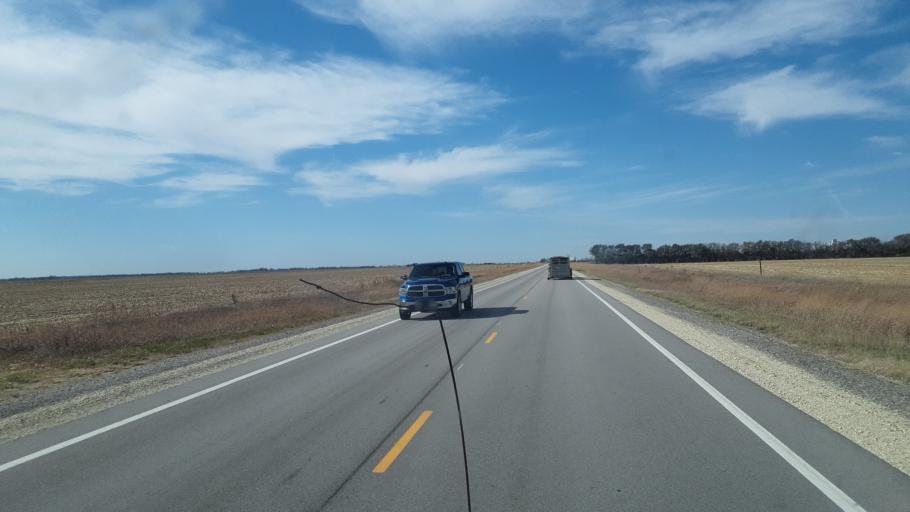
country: US
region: Kansas
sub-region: Marion County
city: Hillsboro
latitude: 38.3770
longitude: -97.3997
